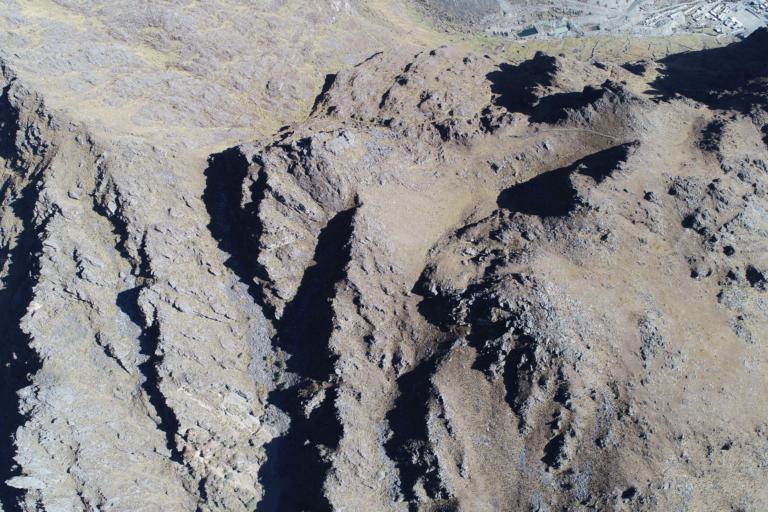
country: BO
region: La Paz
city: Sorata
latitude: -15.6550
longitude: -68.5313
